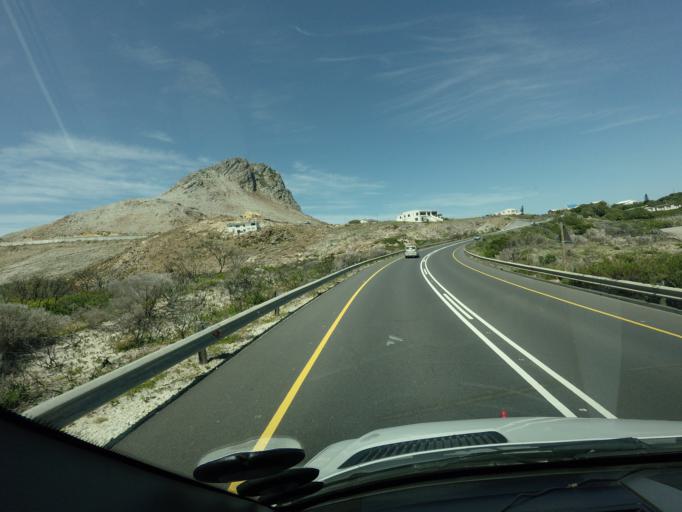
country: ZA
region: Western Cape
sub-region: Overberg District Municipality
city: Grabouw
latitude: -34.2998
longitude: 18.8226
